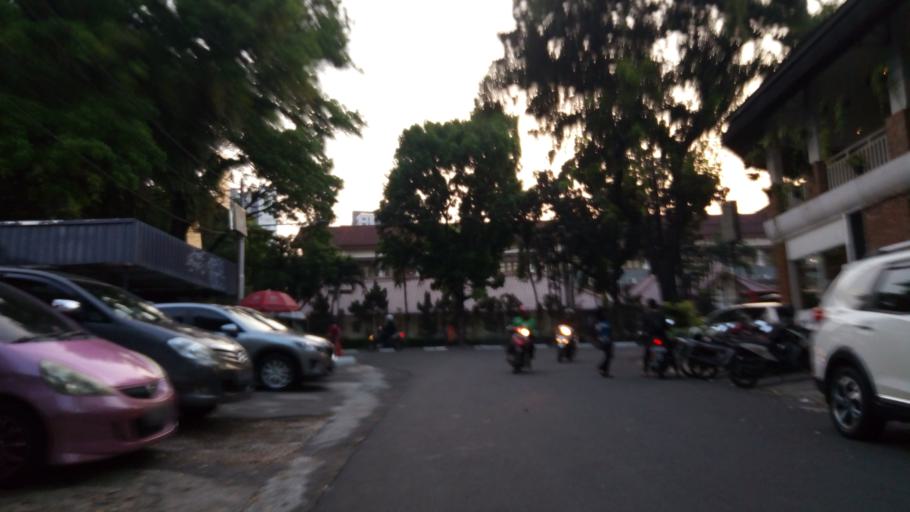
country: ID
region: Jakarta Raya
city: Jakarta
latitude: -6.2452
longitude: 106.7922
